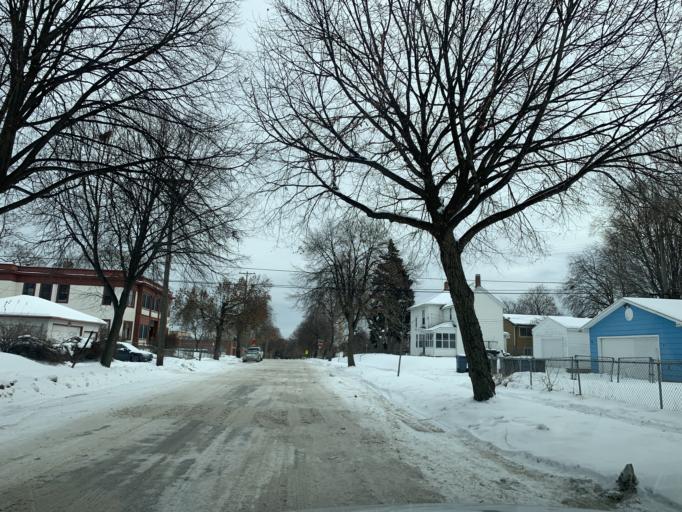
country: US
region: Minnesota
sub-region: Hennepin County
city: Minneapolis
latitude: 44.9952
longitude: -93.2923
